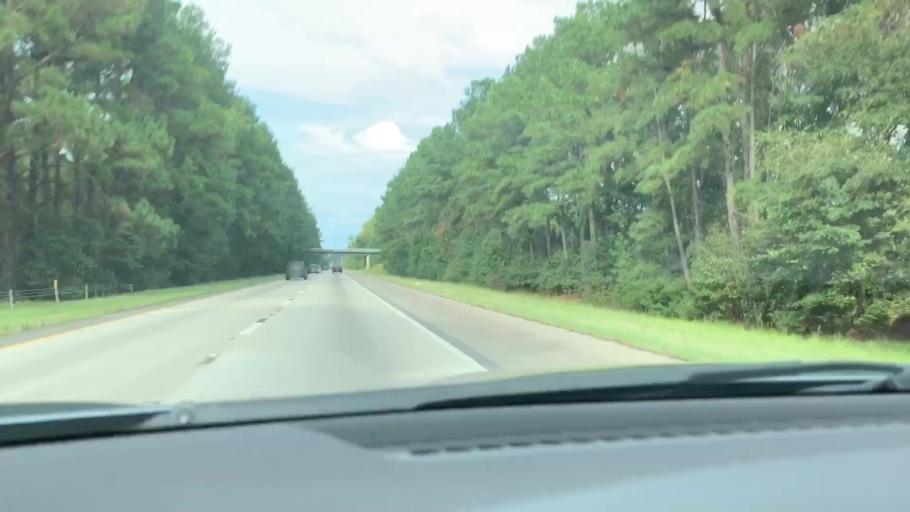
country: US
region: South Carolina
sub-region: Colleton County
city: Walterboro
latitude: 32.8934
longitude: -80.7105
